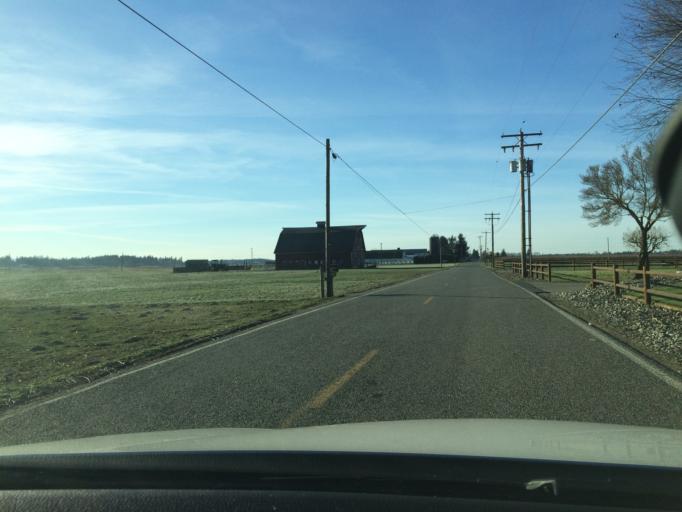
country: US
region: Washington
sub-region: Whatcom County
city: Lynden
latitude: 48.9277
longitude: -122.4157
